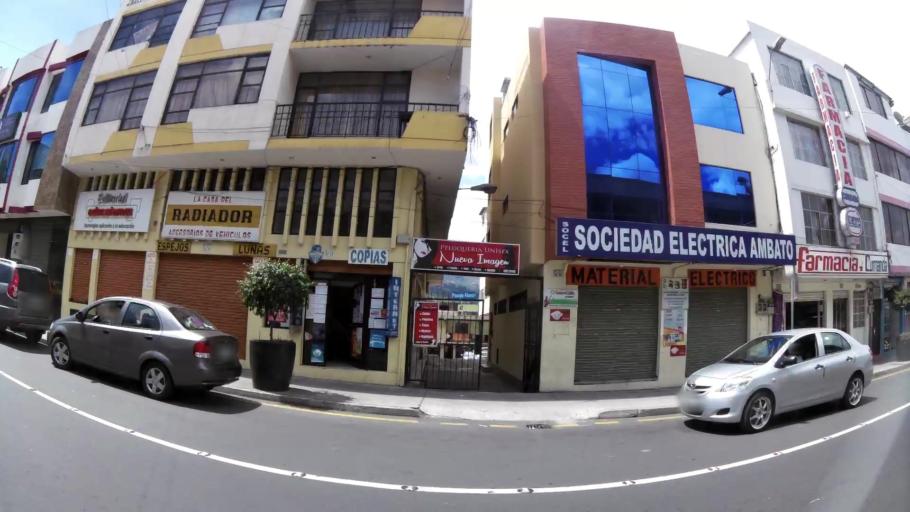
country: EC
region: Tungurahua
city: Ambato
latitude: -1.2370
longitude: -78.6206
